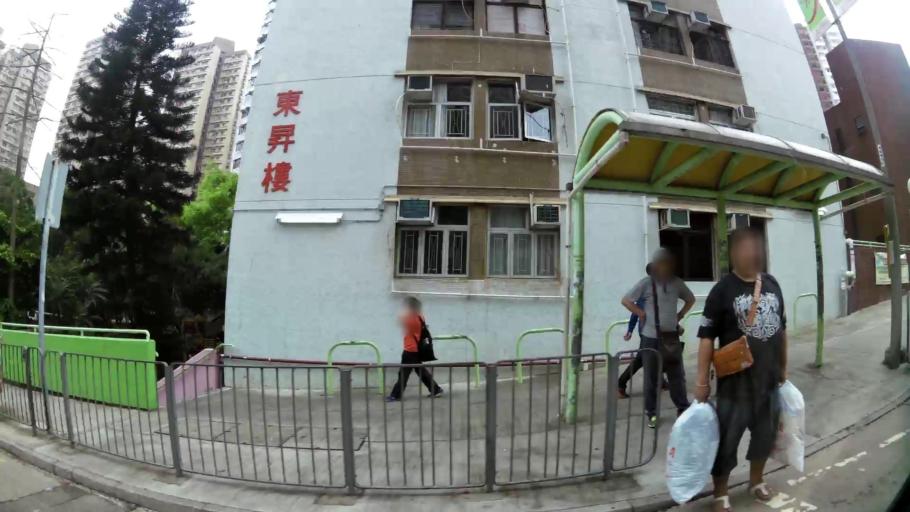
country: HK
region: Central and Western
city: Central
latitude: 22.2415
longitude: 114.1562
